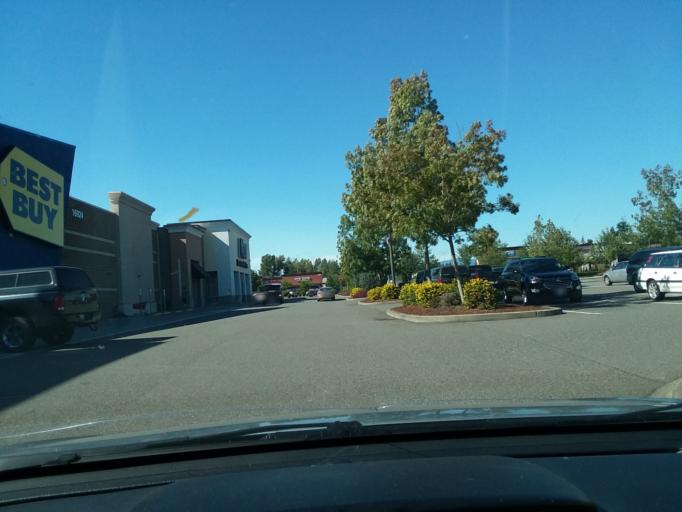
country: US
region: Washington
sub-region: Snohomish County
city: Smokey Point
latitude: 48.1499
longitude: -122.1920
